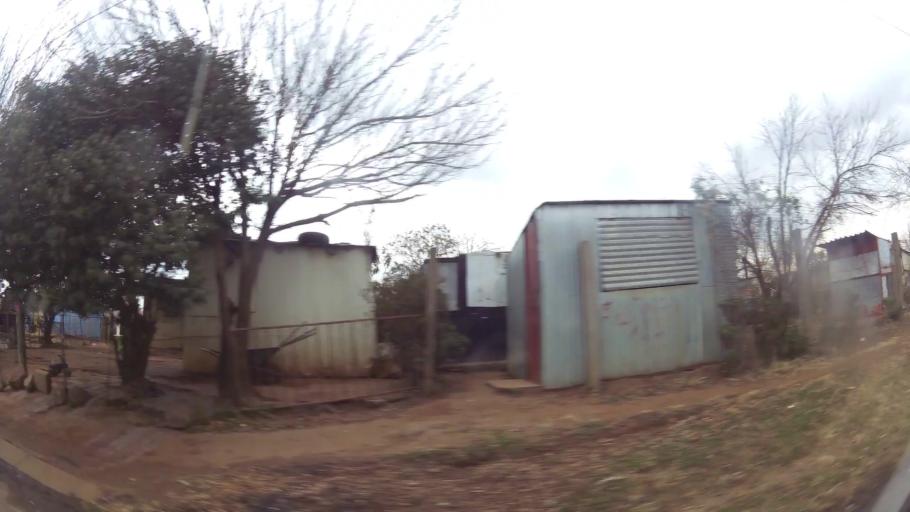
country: ZA
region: Gauteng
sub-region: Ekurhuleni Metropolitan Municipality
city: Germiston
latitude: -26.3638
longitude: 28.1480
